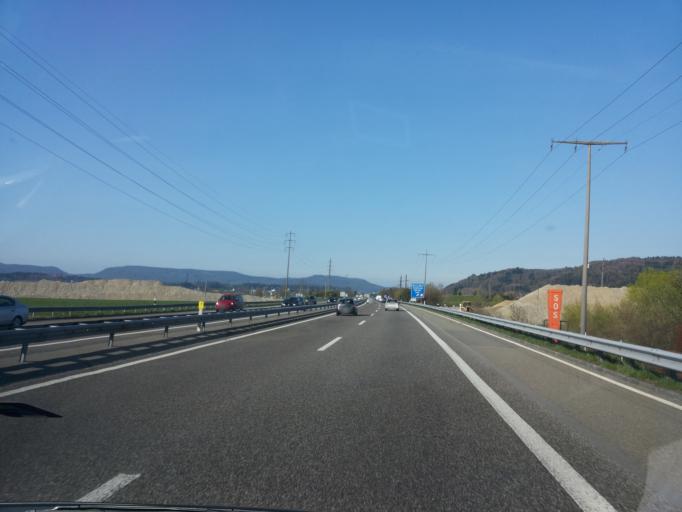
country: CH
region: Aargau
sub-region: Bezirk Zofingen
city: Kolliken
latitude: 47.3346
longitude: 8.0375
